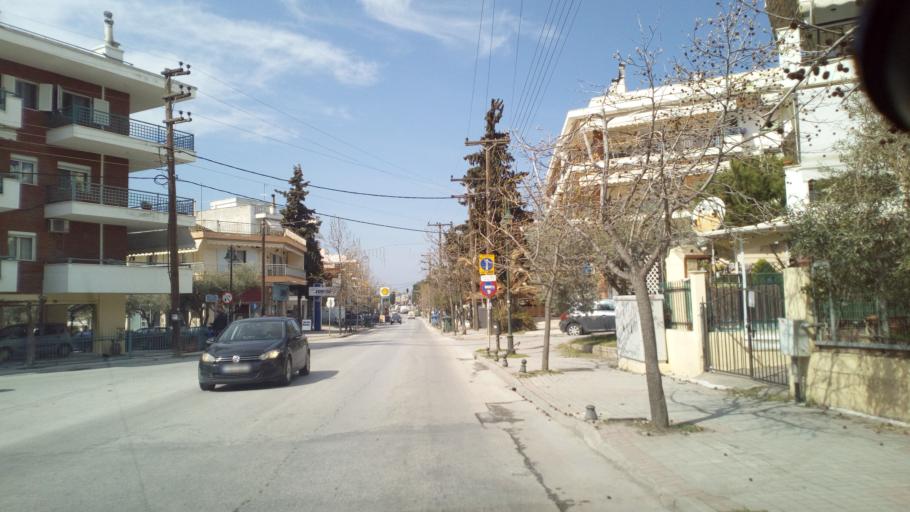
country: GR
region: Central Macedonia
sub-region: Nomos Thessalonikis
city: Thermi
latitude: 40.5511
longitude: 23.0203
